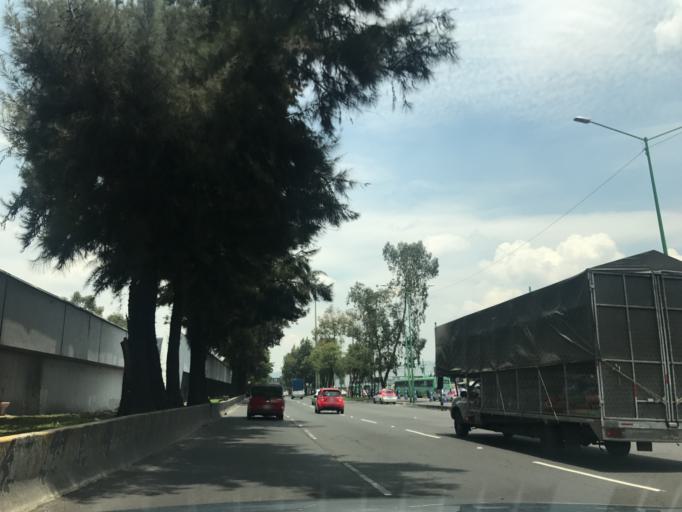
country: MX
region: Mexico
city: Colonia Lindavista
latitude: 19.4782
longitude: -99.1401
